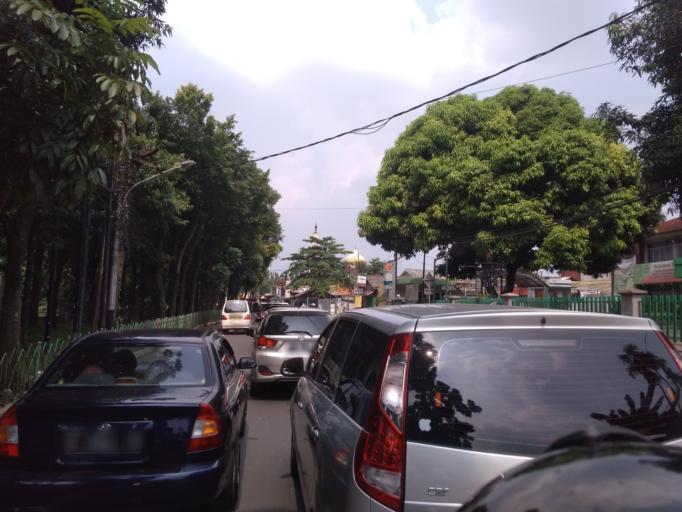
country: ID
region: Banten
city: South Tangerang
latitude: -6.2936
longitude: 106.7721
